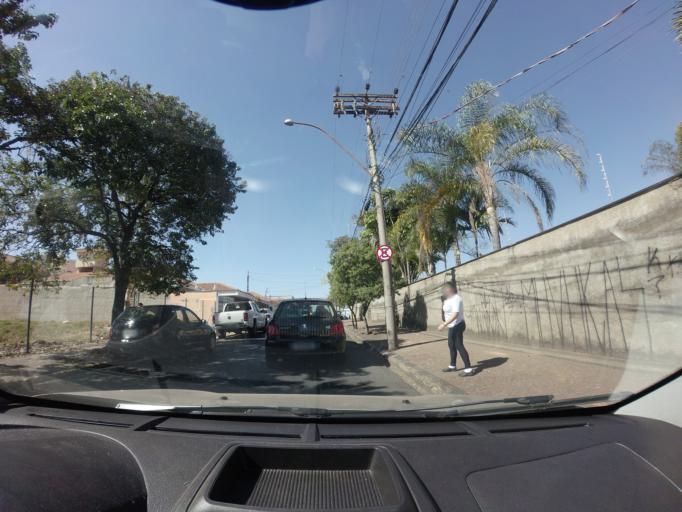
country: BR
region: Sao Paulo
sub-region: Piracicaba
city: Piracicaba
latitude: -22.7243
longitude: -47.6327
